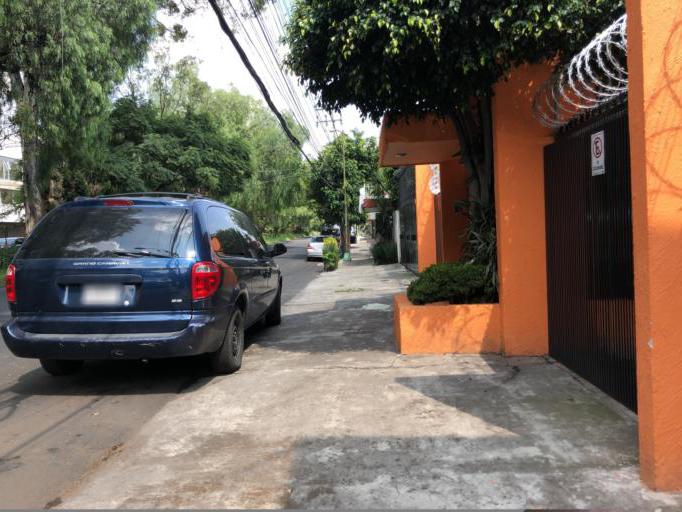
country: MX
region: Mexico City
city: Coyoacan
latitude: 19.3380
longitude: -99.1746
